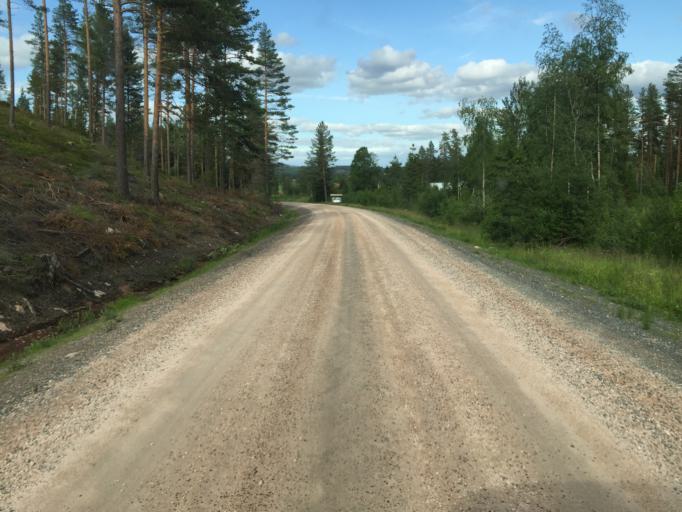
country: SE
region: Dalarna
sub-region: Malung-Saelens kommun
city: Malung
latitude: 60.9439
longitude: 13.8862
